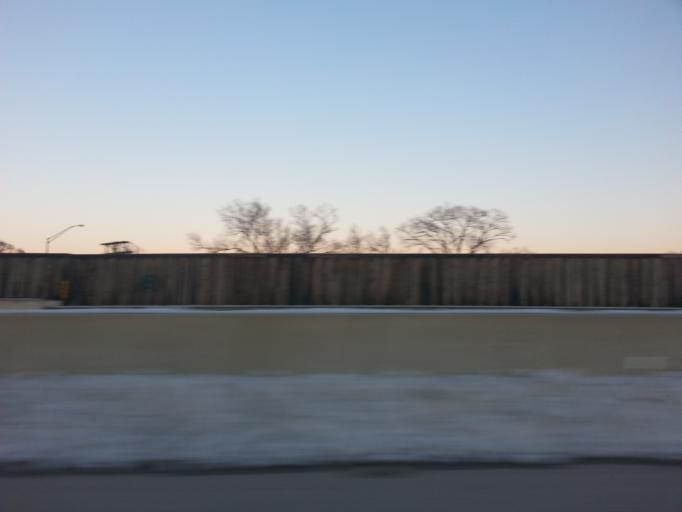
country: US
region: Illinois
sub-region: Cook County
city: Chicago Ridge
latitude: 41.6899
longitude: -87.7829
